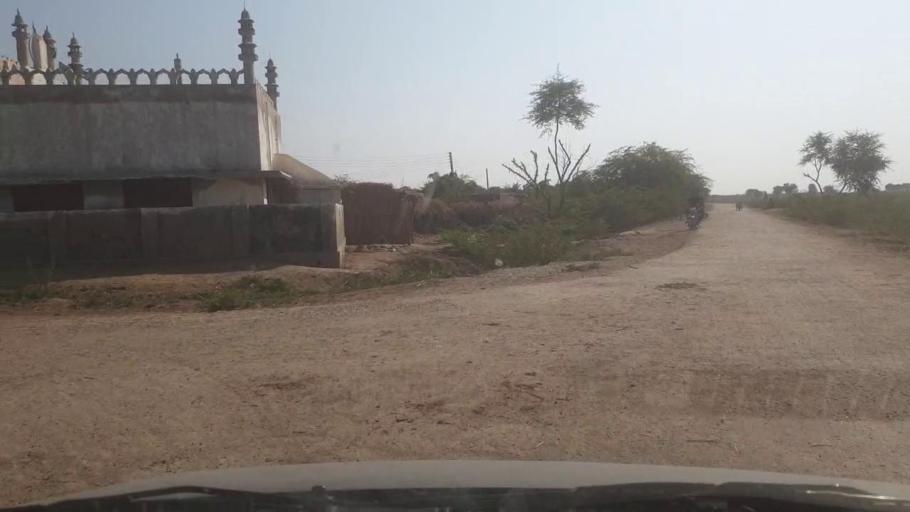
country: PK
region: Sindh
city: Samaro
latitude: 25.1838
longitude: 69.3657
